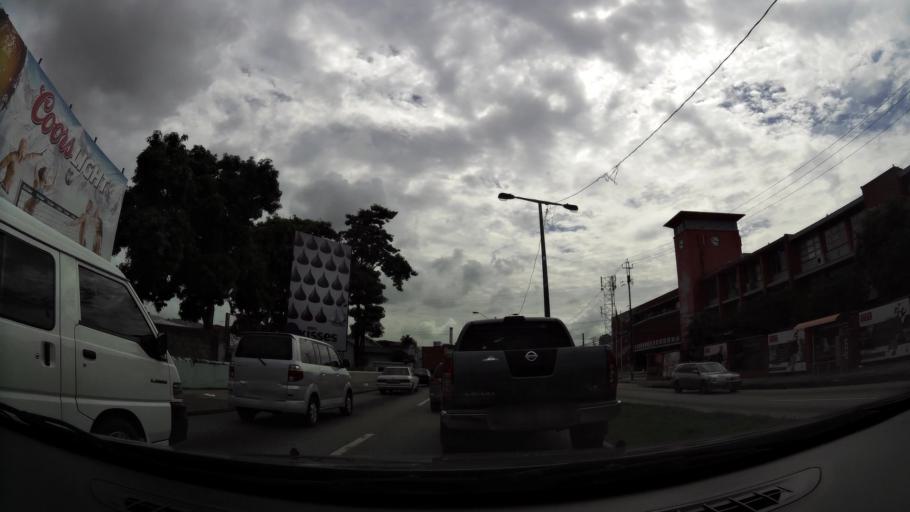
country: TT
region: City of Port of Spain
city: Port-of-Spain
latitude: 10.6587
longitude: -61.5226
